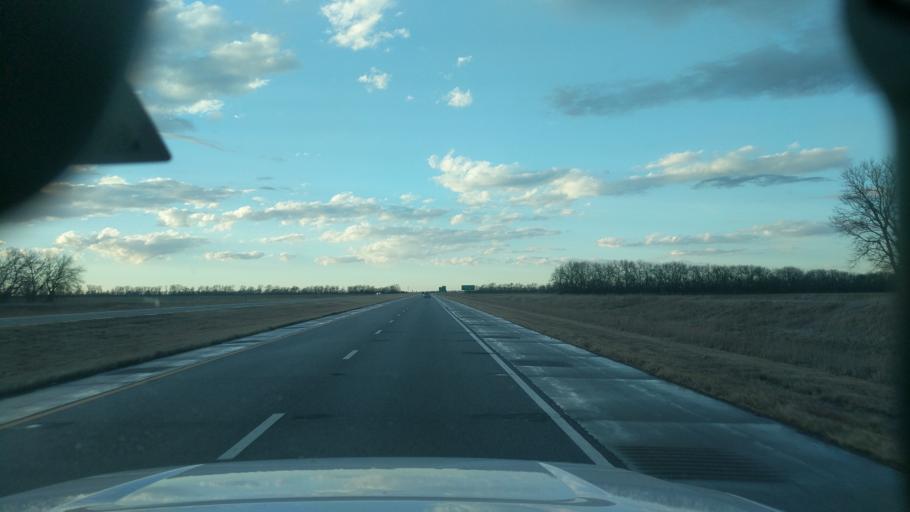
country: US
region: Kansas
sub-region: McPherson County
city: Moundridge
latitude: 38.1900
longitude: -97.4711
